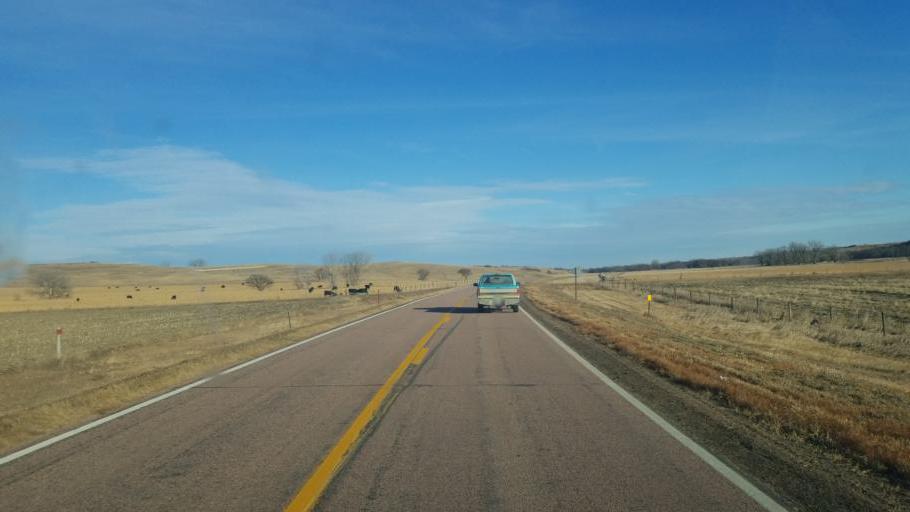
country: US
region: South Dakota
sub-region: Charles Mix County
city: Wagner
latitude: 42.8299
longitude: -98.4488
